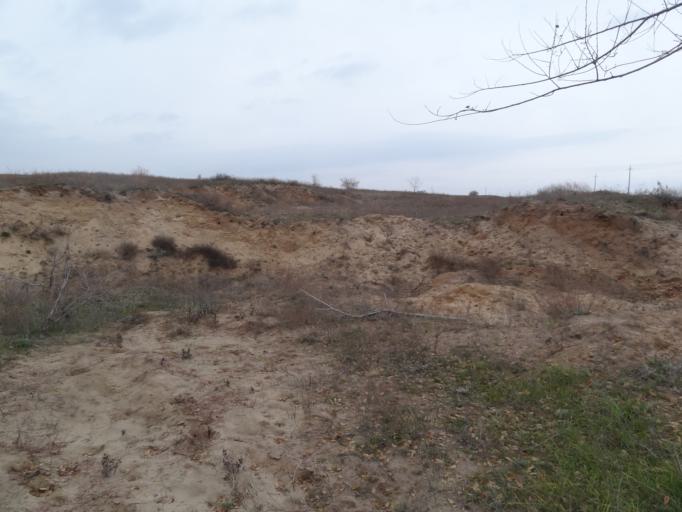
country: RU
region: Saratov
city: Sovetskoye
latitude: 51.5474
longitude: 46.6100
